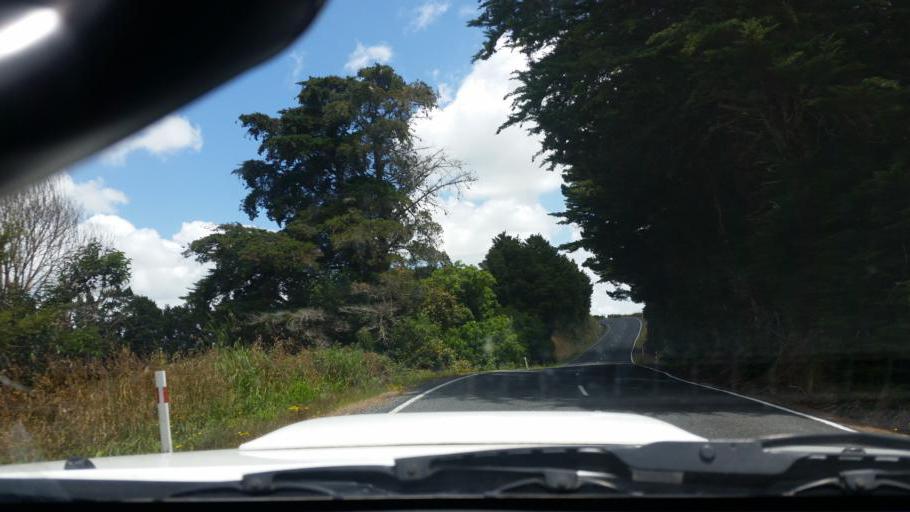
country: NZ
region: Northland
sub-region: Whangarei
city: Ruakaka
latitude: -36.0469
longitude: 174.2772
